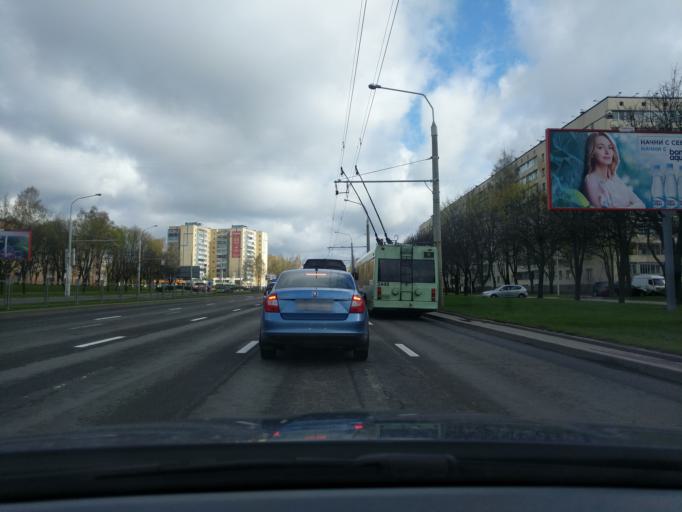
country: BY
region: Minsk
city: Novoye Medvezhino
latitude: 53.9136
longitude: 27.4952
